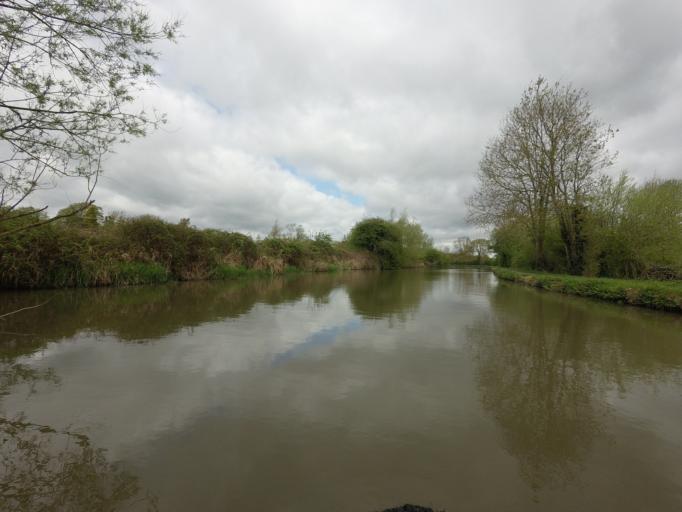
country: GB
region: England
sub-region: Milton Keynes
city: Water Eaton
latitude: 51.9635
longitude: -0.7148
